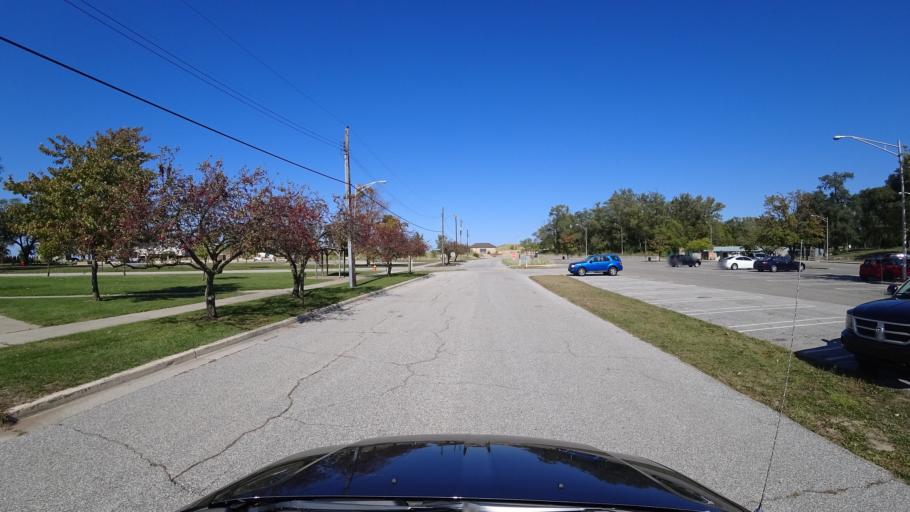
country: US
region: Indiana
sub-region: LaPorte County
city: Michigan City
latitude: 41.7258
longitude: -86.9018
